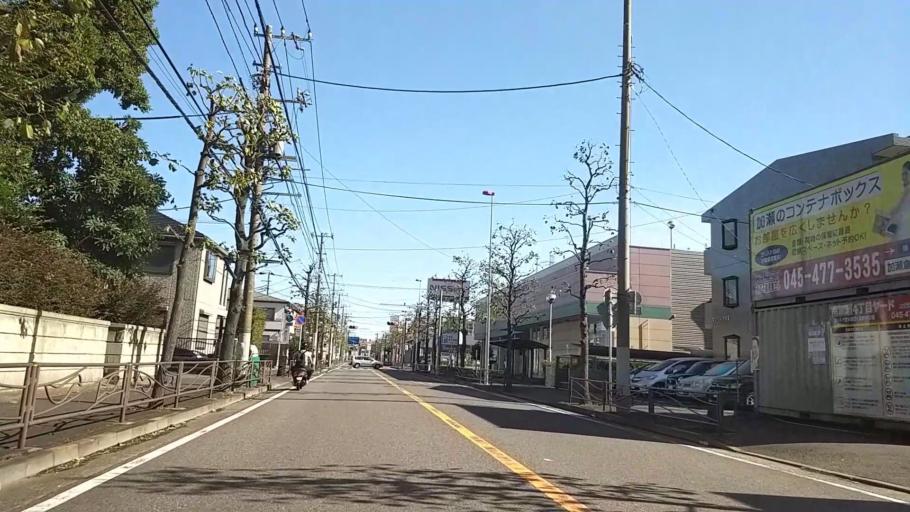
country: JP
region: Kanagawa
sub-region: Kawasaki-shi
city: Kawasaki
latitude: 35.5466
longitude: 139.6581
